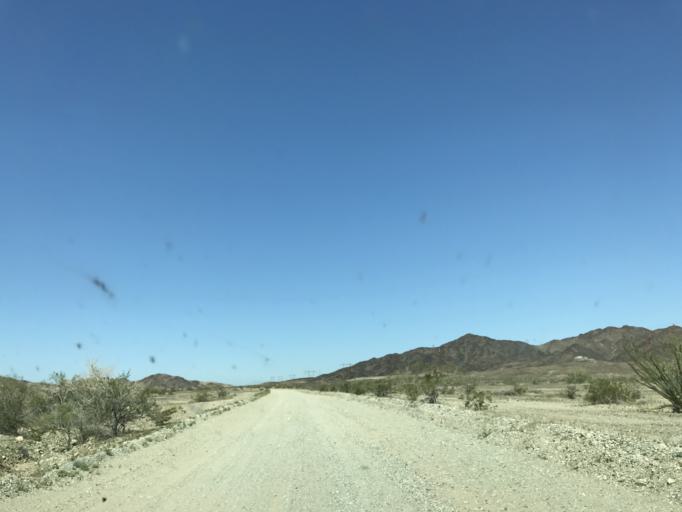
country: US
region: California
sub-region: Riverside County
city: Mesa Verde
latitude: 33.4930
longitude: -114.8139
